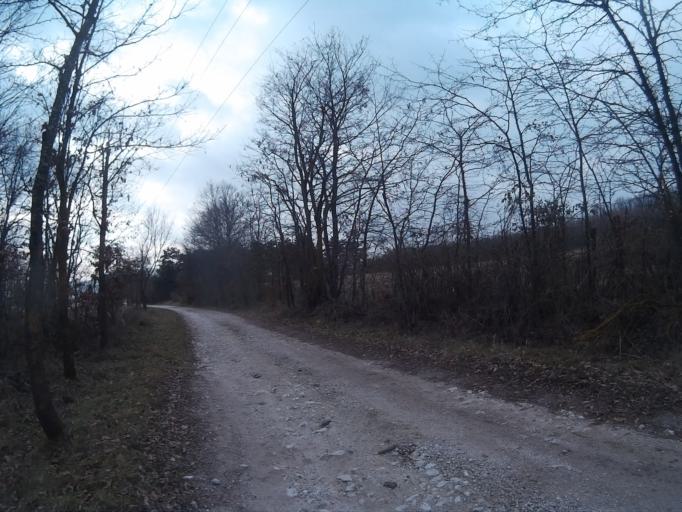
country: HU
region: Veszprem
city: Tapolca
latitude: 46.9423
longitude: 17.4867
